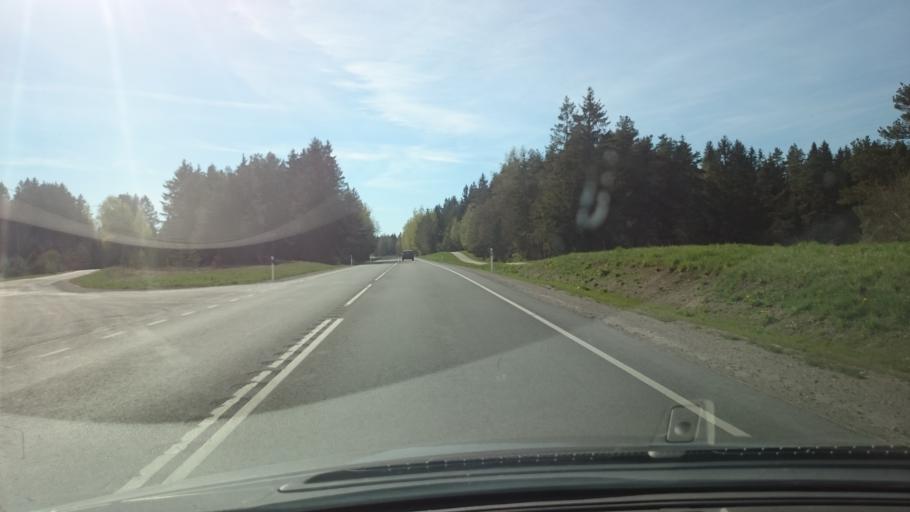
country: EE
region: Laeaene-Virumaa
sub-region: Kadrina vald
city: Kadrina
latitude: 59.3555
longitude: 26.1945
